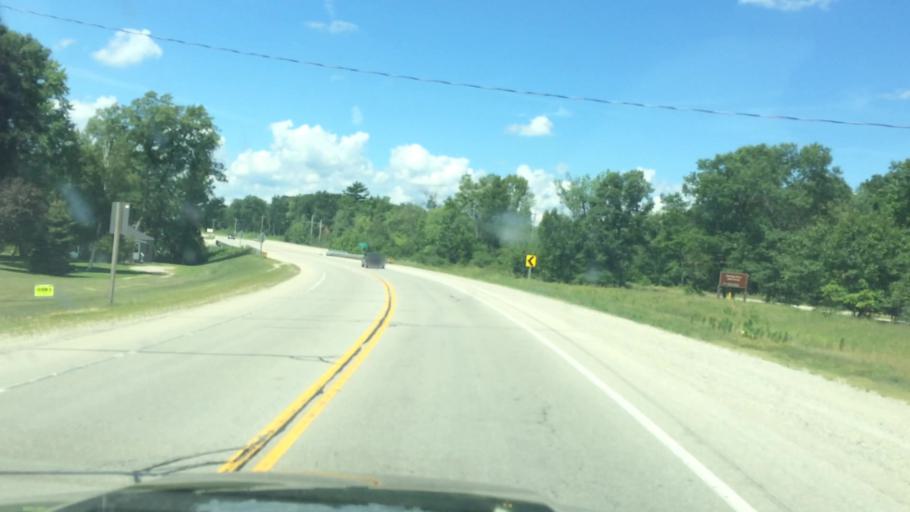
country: US
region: Wisconsin
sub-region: Marinette County
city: Peshtigo
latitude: 45.1062
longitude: -87.7525
